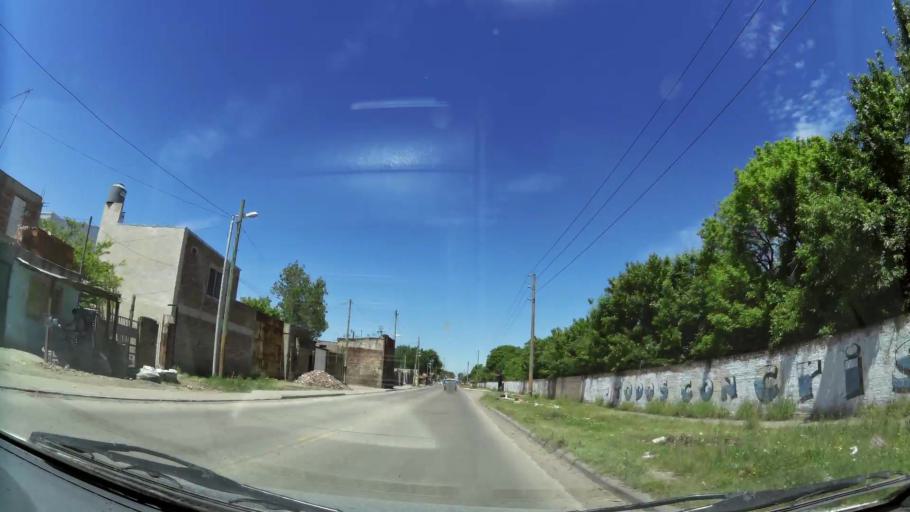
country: AR
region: Buenos Aires
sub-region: Partido de Lanus
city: Lanus
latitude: -34.7287
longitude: -58.3316
